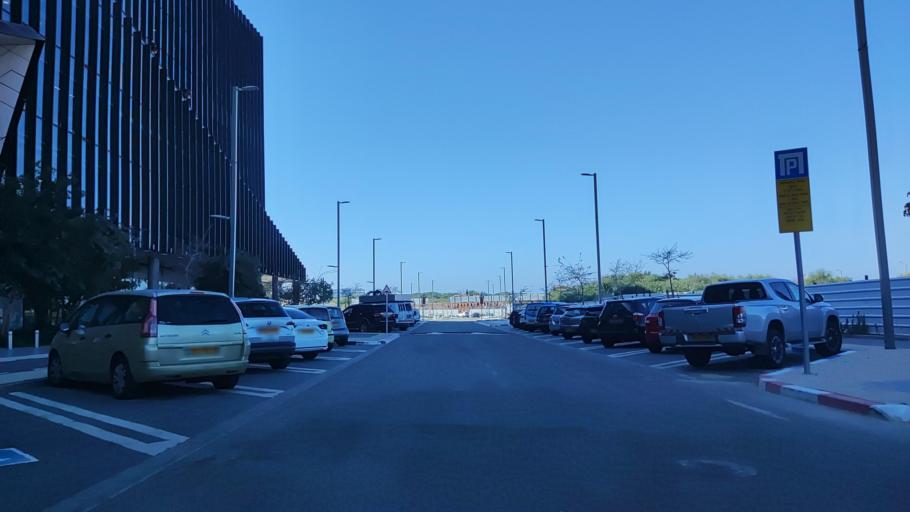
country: IL
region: Tel Aviv
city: Herzliya Pituah
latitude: 32.1571
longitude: 34.8056
